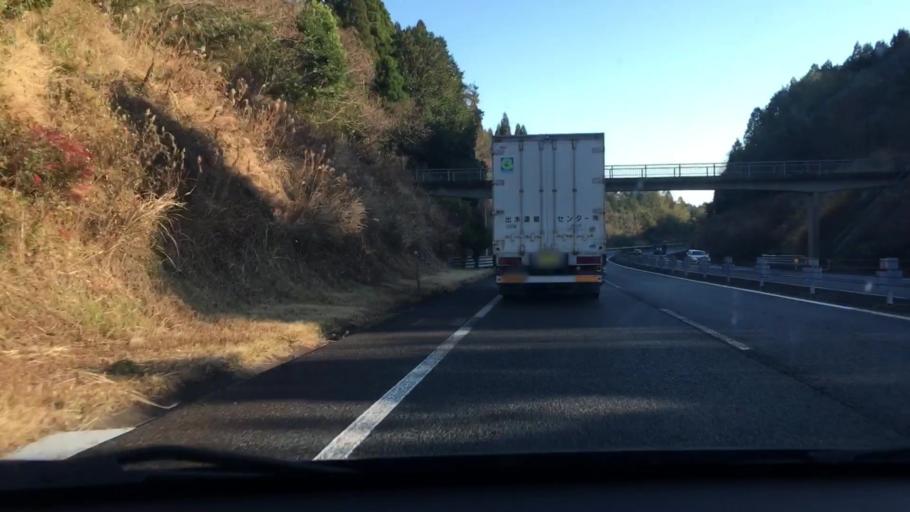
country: JP
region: Kagoshima
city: Kajiki
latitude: 31.8329
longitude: 130.6918
